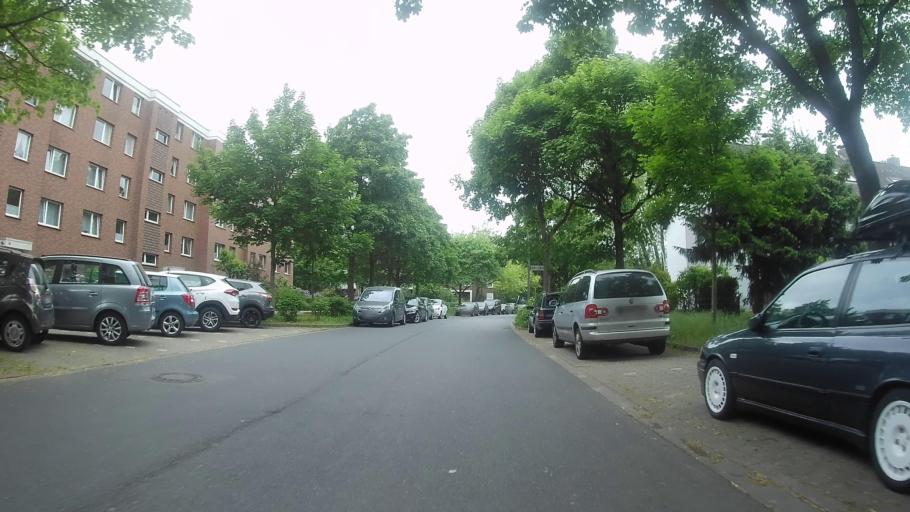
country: DE
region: Hamburg
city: Steilshoop
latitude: 53.6165
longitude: 10.0668
